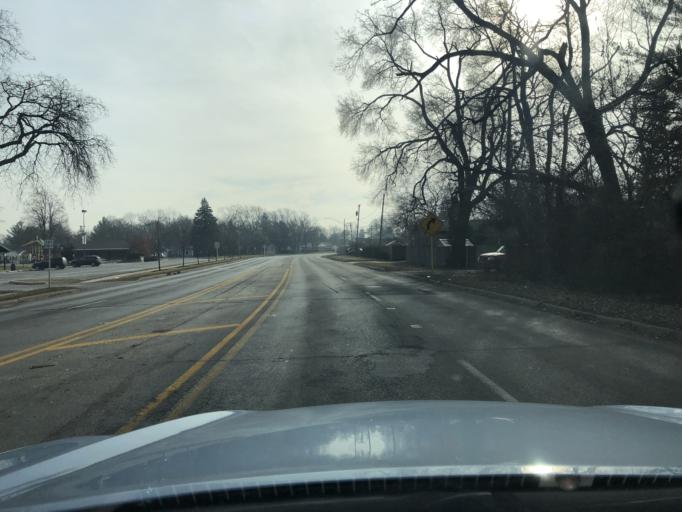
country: US
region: Illinois
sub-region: Cook County
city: Des Plaines
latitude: 42.0416
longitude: -87.9110
